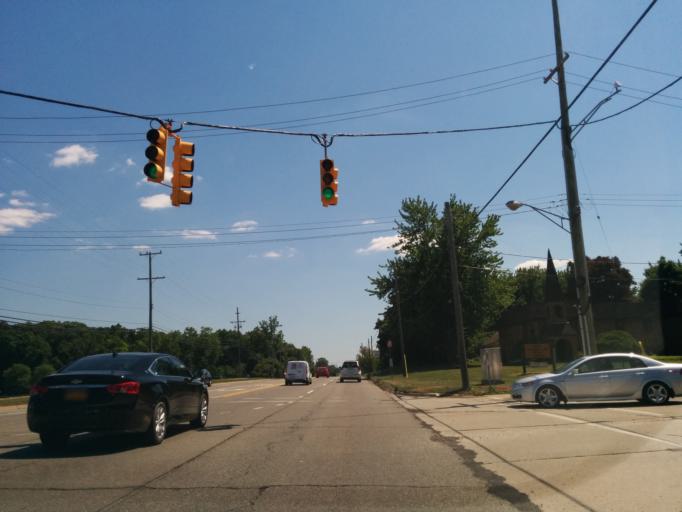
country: US
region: Michigan
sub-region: Oakland County
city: Orchard Lake
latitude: 42.5669
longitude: -83.3619
